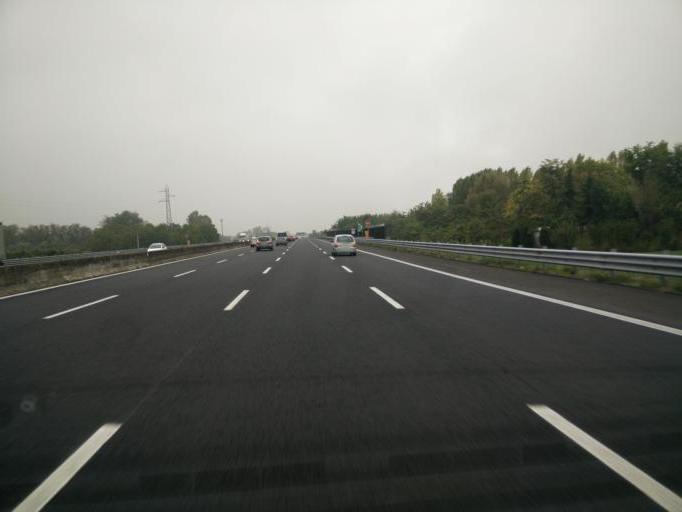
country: IT
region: Emilia-Romagna
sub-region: Provincia di Modena
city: San Damaso
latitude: 44.5959
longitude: 10.9380
